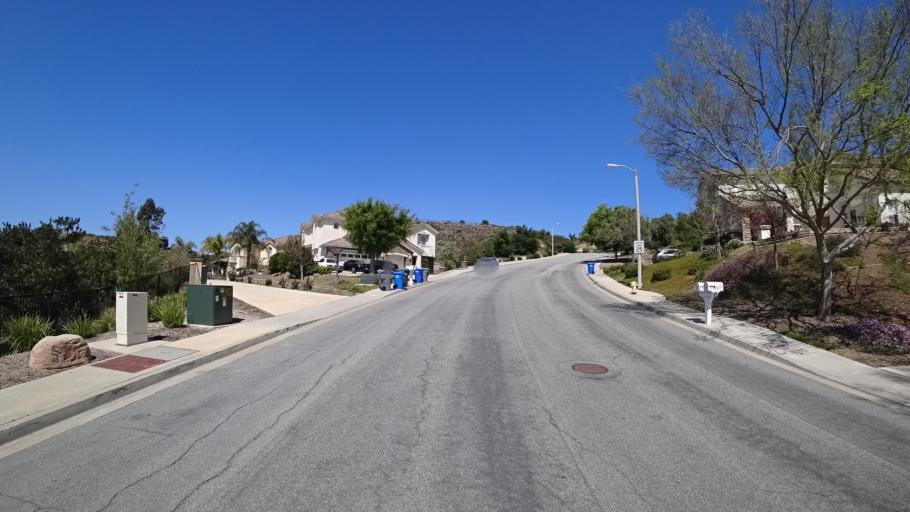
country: US
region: California
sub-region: Ventura County
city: Moorpark
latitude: 34.2301
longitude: -118.8818
